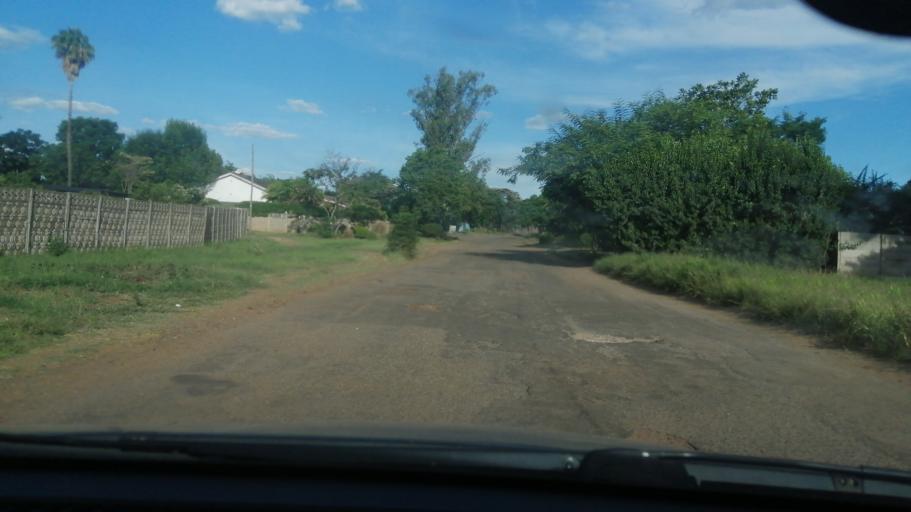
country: ZW
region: Harare
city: Harare
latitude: -17.7637
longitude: 31.0650
